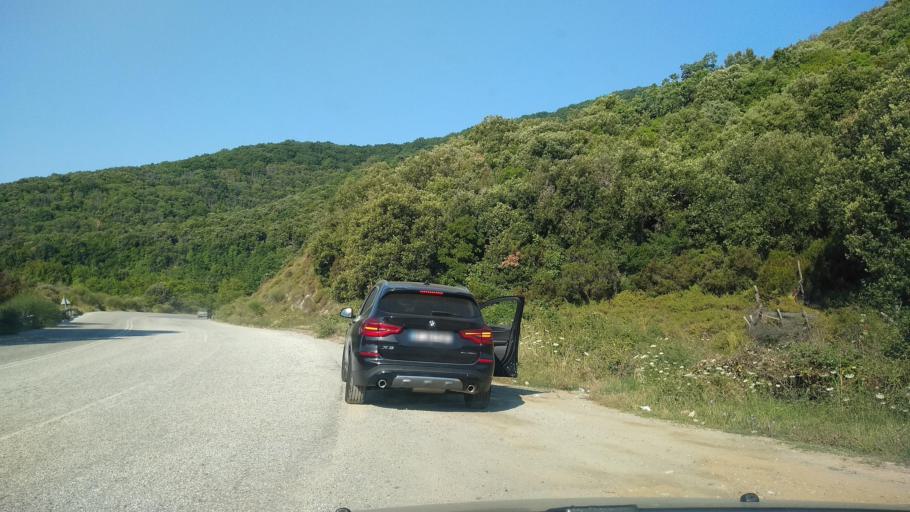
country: GR
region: Central Macedonia
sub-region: Nomos Chalkidikis
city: Stratonion
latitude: 40.5310
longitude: 23.8261
